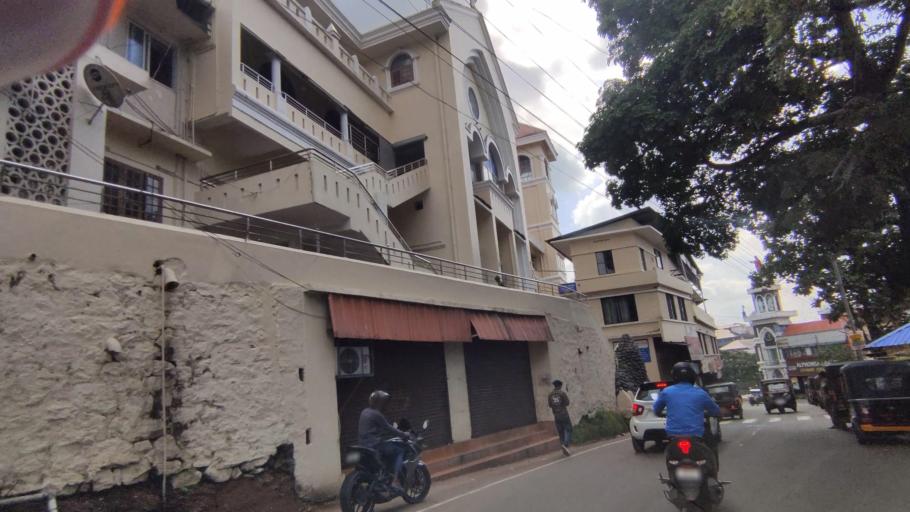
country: IN
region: Kerala
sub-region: Kottayam
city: Kottayam
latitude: 9.6702
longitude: 76.5559
